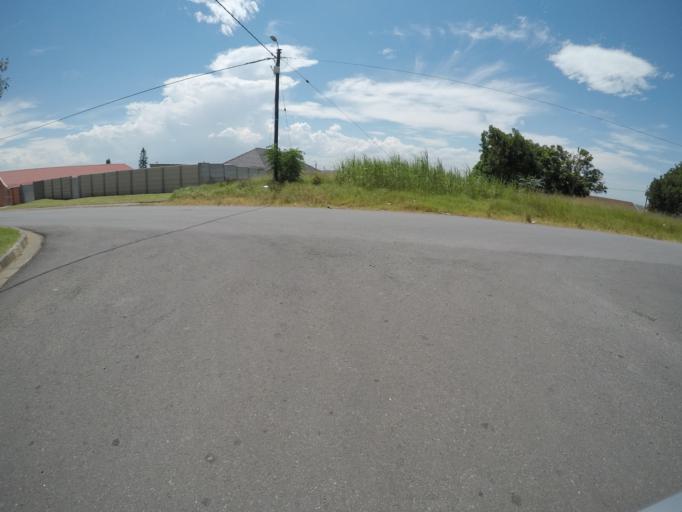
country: ZA
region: Eastern Cape
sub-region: Buffalo City Metropolitan Municipality
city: East London
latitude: -33.0323
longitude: 27.8527
